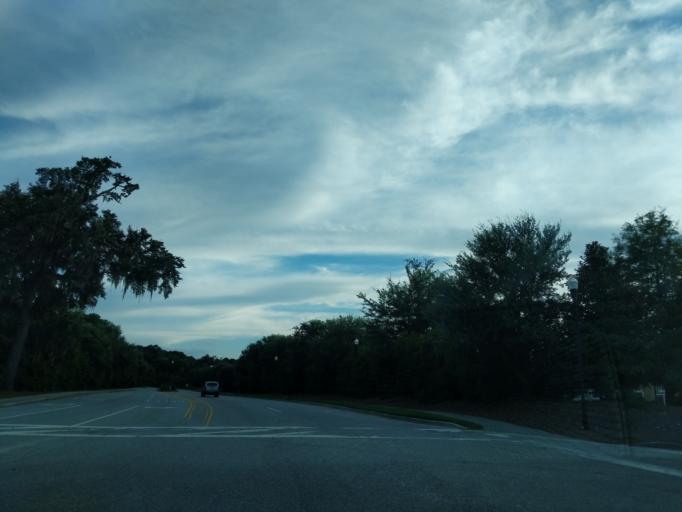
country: US
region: South Carolina
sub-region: Charleston County
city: Isle of Palms
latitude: 32.8370
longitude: -79.8167
